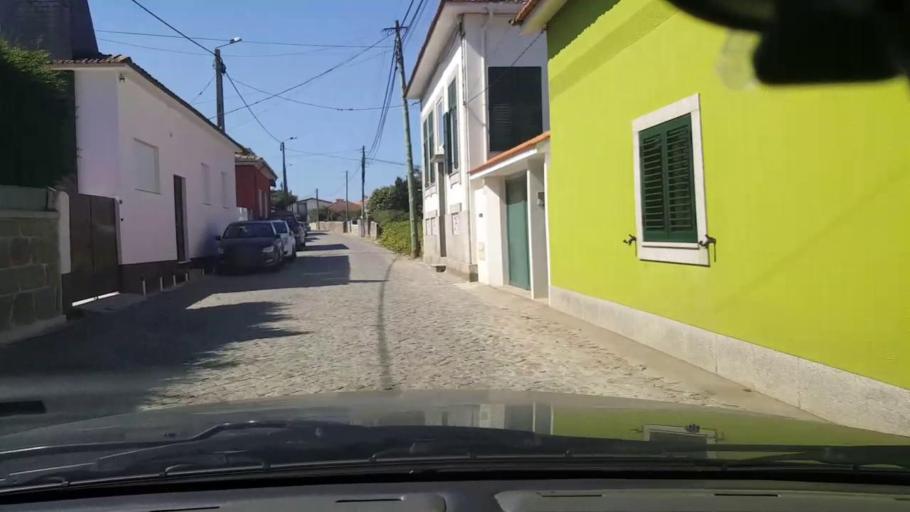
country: PT
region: Porto
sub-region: Matosinhos
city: Lavra
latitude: 41.2668
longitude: -8.6972
